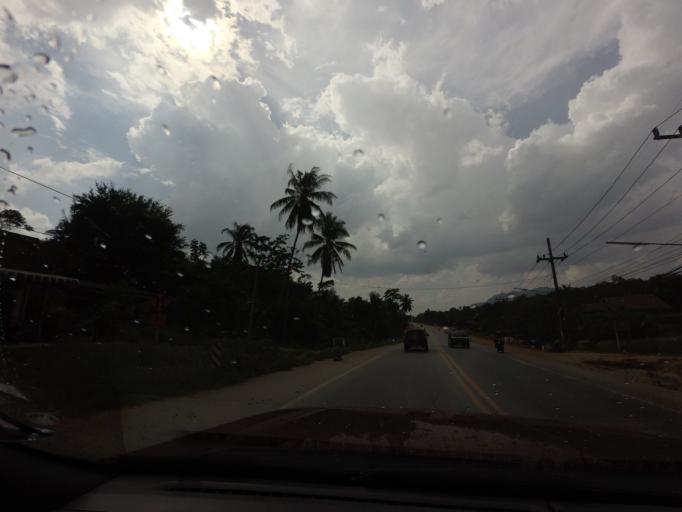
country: TH
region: Yala
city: Krong Pi Nang
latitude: 6.4022
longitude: 101.2819
